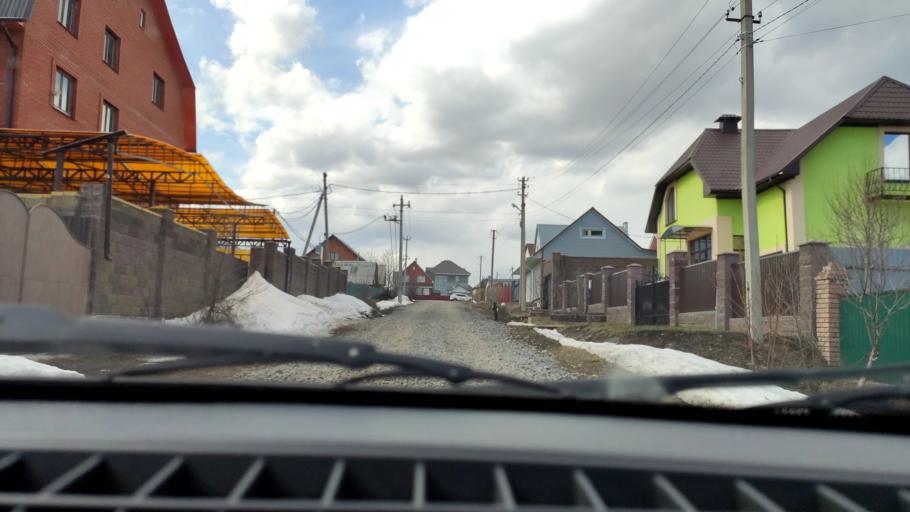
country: RU
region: Bashkortostan
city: Mikhaylovka
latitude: 54.8220
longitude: 55.8953
